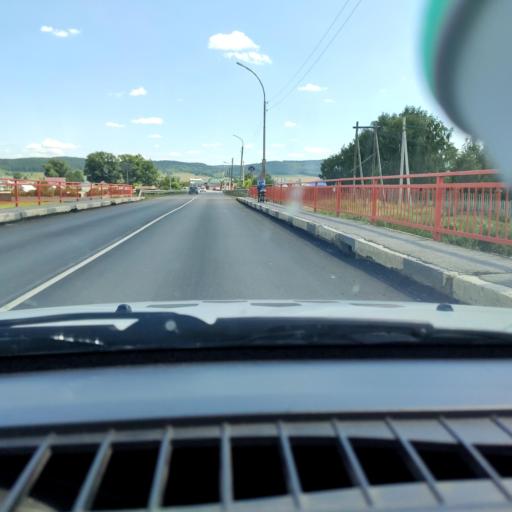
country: RU
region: Bashkortostan
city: Mesyagutovo
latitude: 55.5309
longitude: 58.2538
